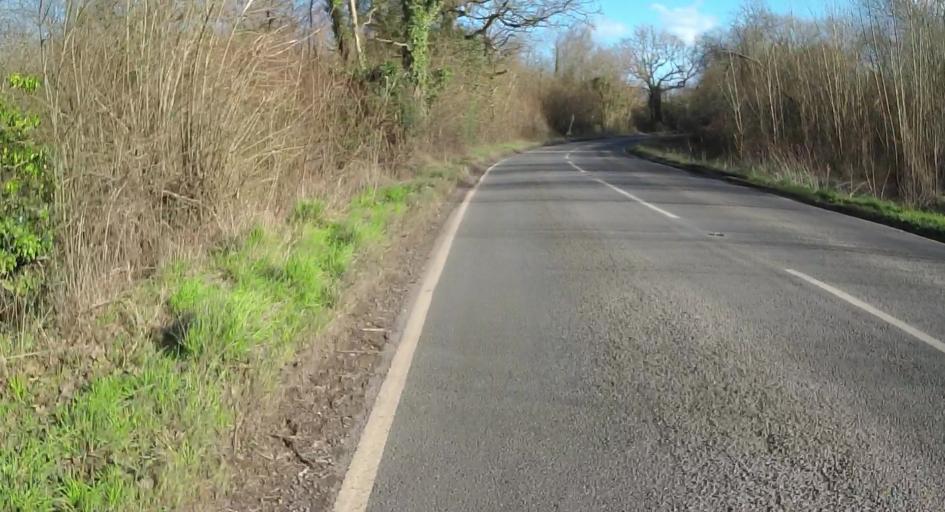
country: GB
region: England
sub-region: Hampshire
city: Kings Worthy
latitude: 51.0878
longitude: -1.1907
